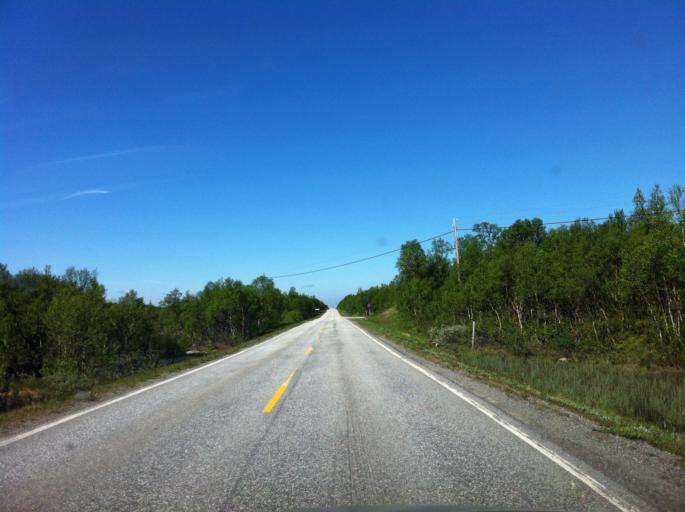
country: NO
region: Sor-Trondelag
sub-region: Tydal
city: Aas
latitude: 62.6376
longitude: 11.9968
